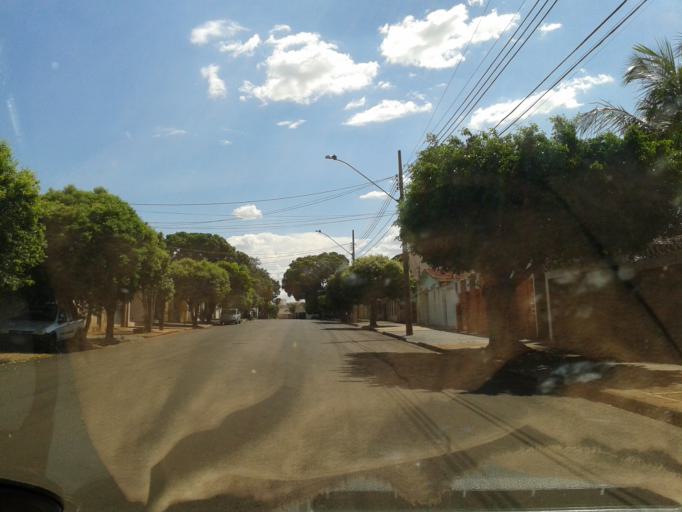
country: BR
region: Minas Gerais
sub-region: Ituiutaba
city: Ituiutaba
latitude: -18.9866
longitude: -49.4561
